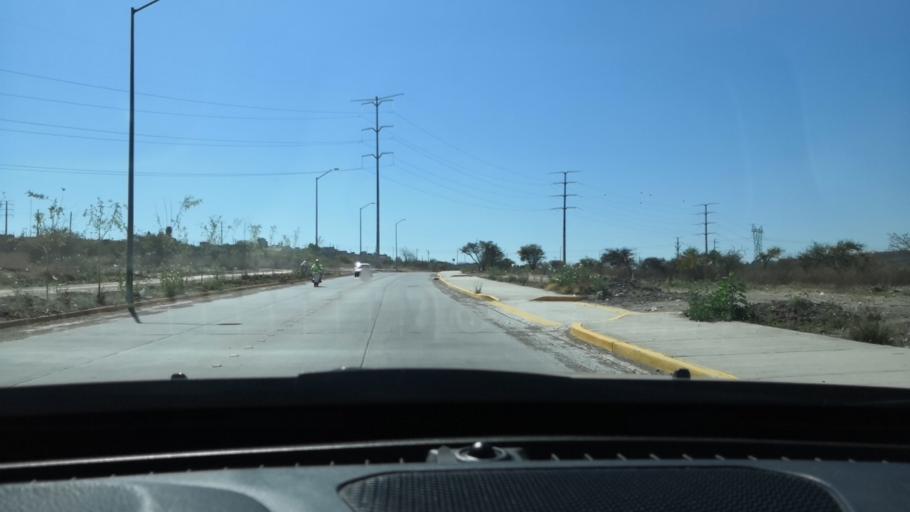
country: MX
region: Guanajuato
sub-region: Leon
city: Ejido la Joya
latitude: 21.1296
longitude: -101.7346
